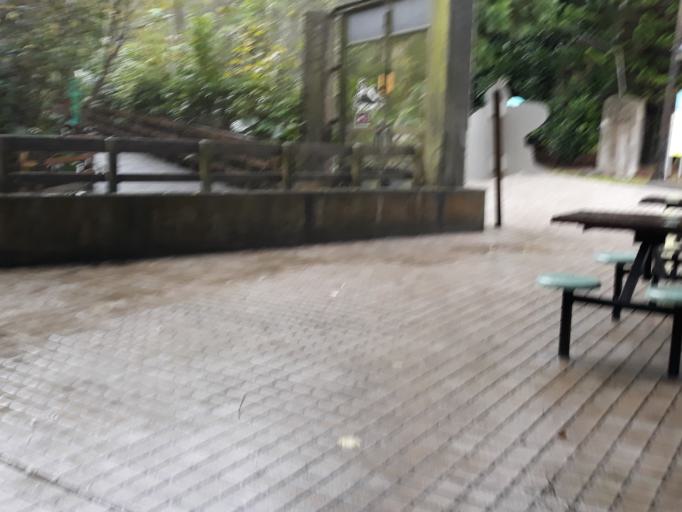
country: TW
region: Taipei
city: Taipei
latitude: 24.9953
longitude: 121.5896
